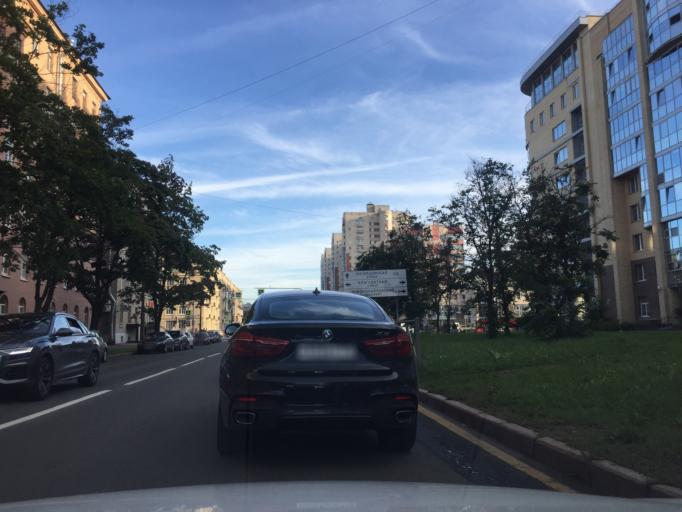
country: RU
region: St.-Petersburg
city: Admiralteisky
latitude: 59.8768
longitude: 30.3133
